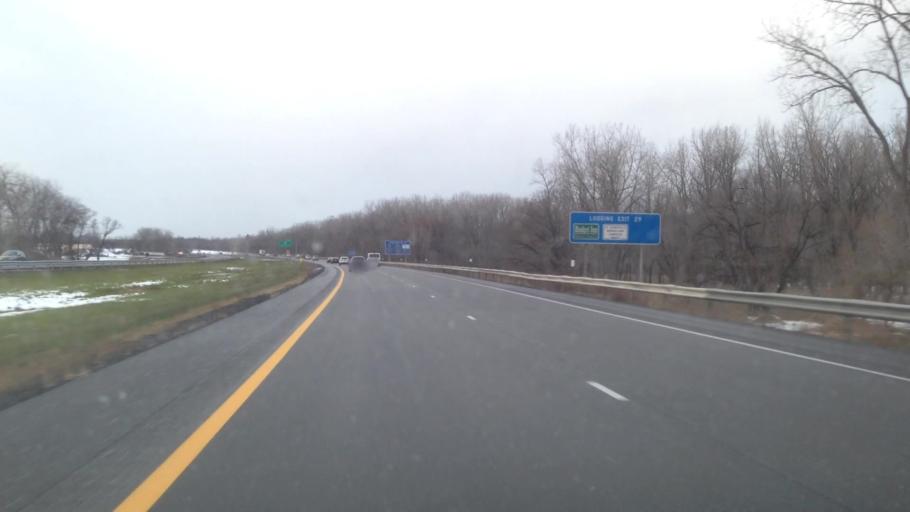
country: US
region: New York
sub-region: Montgomery County
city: Canajoharie
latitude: 42.9029
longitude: -74.5488
